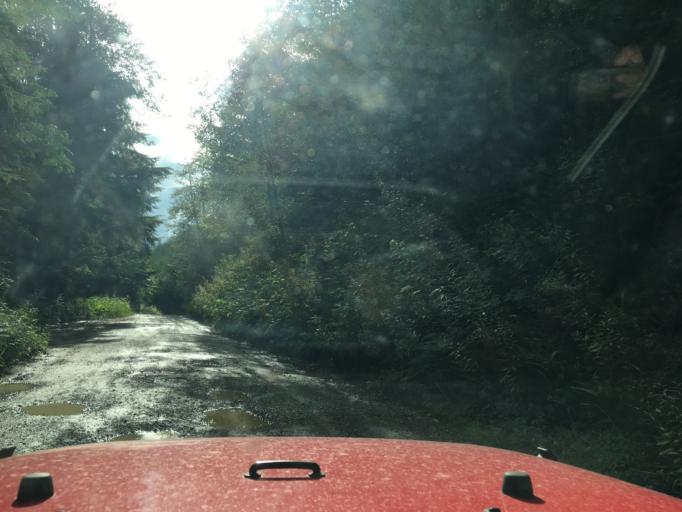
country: US
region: Washington
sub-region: King County
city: Tanner
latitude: 47.6408
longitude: -121.6865
